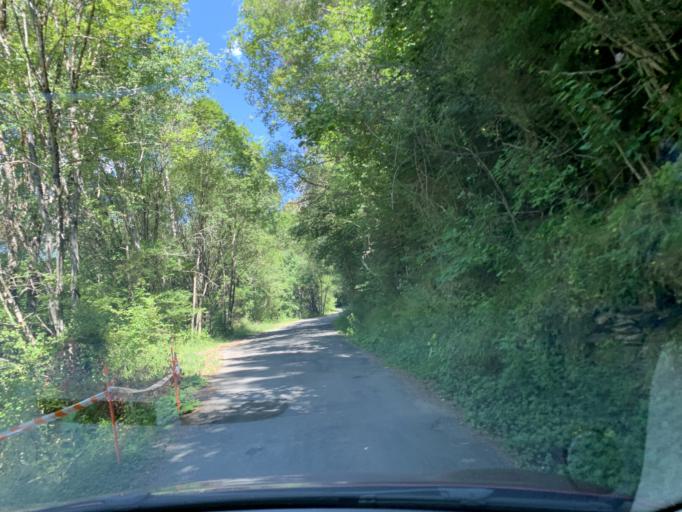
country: ES
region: Aragon
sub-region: Provincia de Huesca
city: Hoz de Jaca
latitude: 42.6976
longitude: -0.3092
